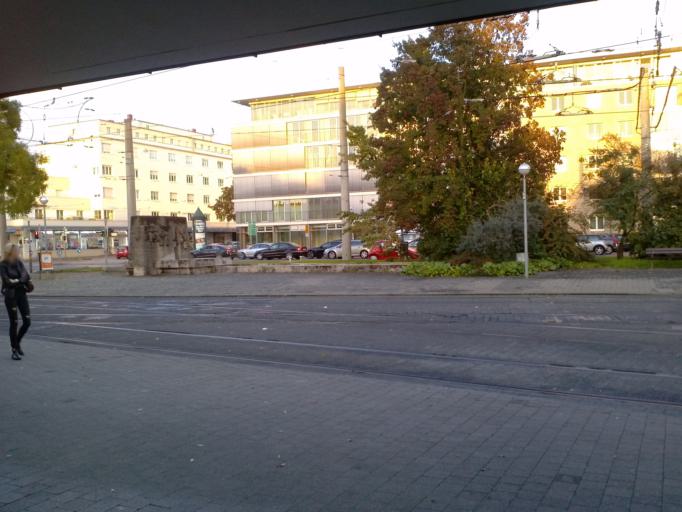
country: DE
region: Baden-Wuerttemberg
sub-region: Karlsruhe Region
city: Karlsruhe
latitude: 48.9940
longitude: 8.3960
